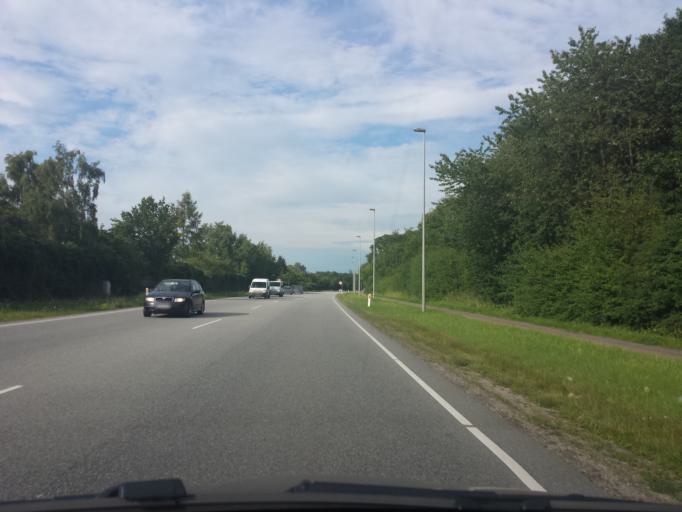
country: DK
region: Capital Region
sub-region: Ballerup Kommune
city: Ballerup
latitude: 55.7371
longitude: 12.3791
